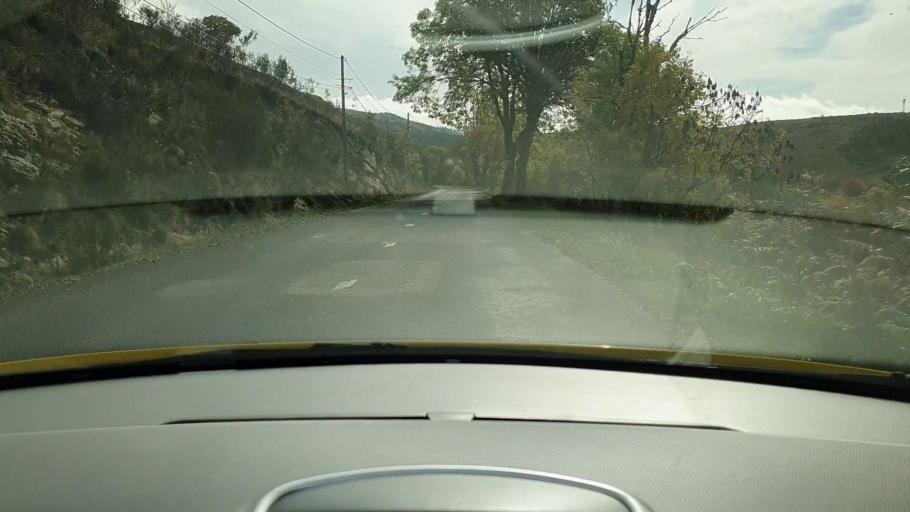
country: FR
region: Languedoc-Roussillon
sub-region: Departement de la Lozere
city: Meyrueis
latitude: 44.0775
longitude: 3.4747
